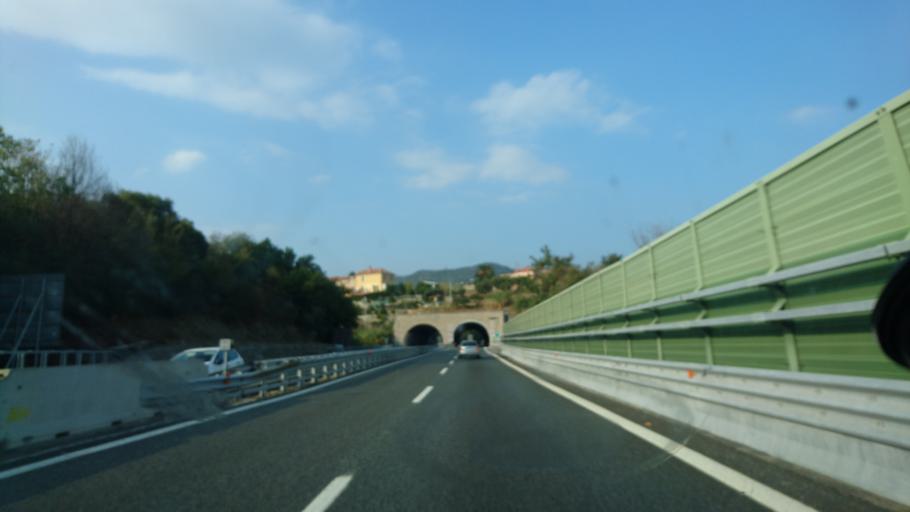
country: IT
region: Liguria
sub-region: Provincia di Savona
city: Valleggia
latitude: 44.2962
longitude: 8.4464
